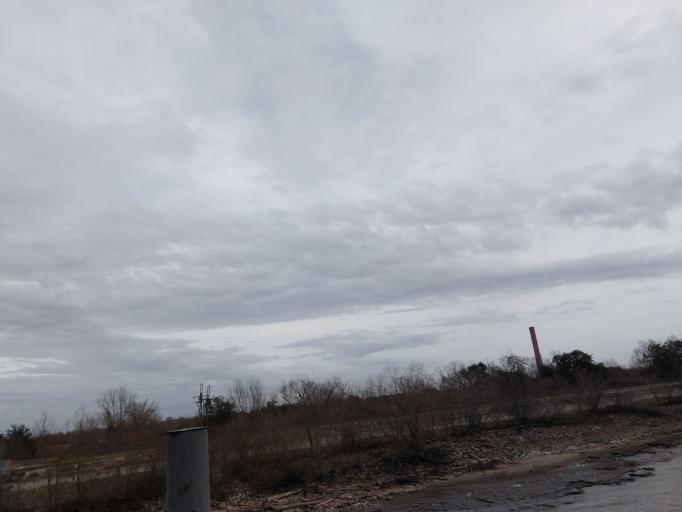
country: US
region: Louisiana
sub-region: Saint Bernard Parish
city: Arabi
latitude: 29.9391
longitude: -89.9942
